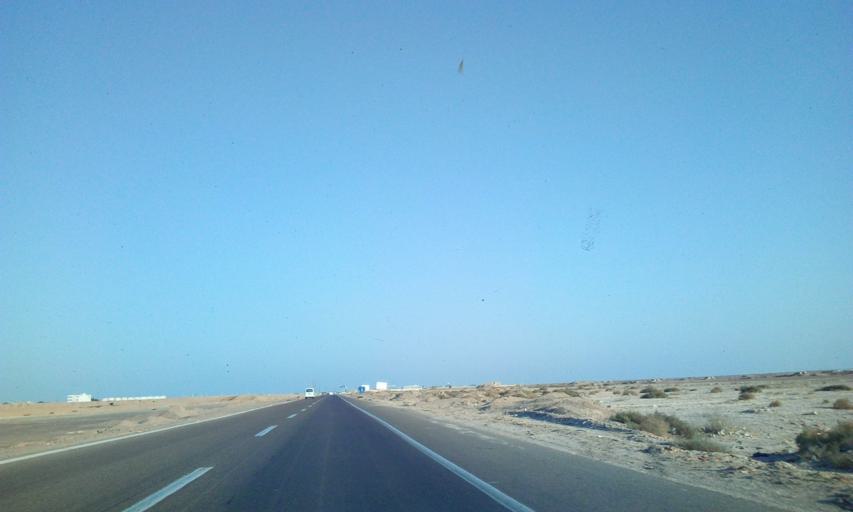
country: EG
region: South Sinai
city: Tor
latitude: 28.3551
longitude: 33.0436
